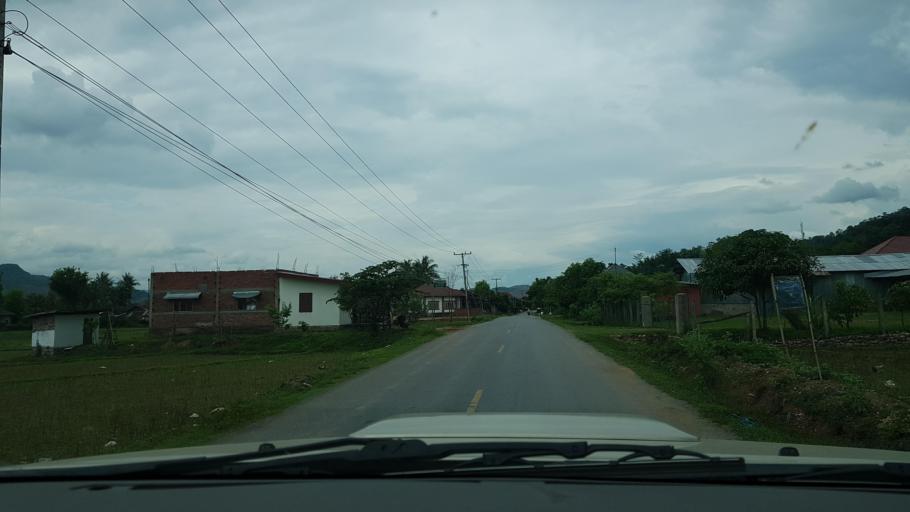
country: LA
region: Loungnamtha
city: Muang Nale
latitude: 20.3372
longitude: 101.6739
